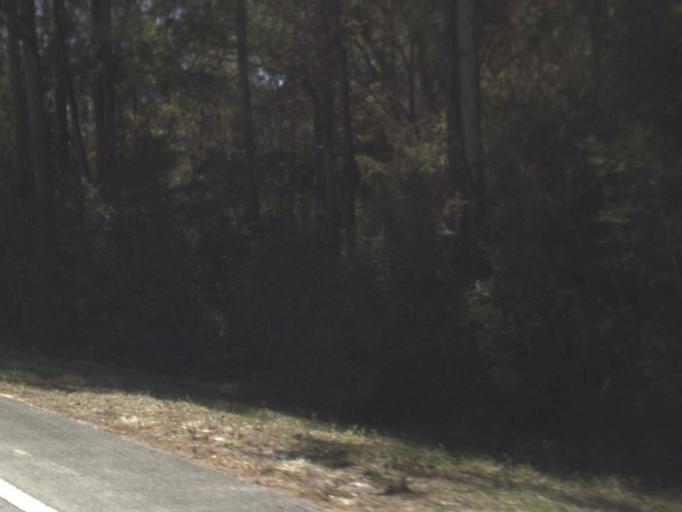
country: US
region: Florida
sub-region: Leon County
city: Woodville
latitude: 30.2087
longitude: -84.2219
